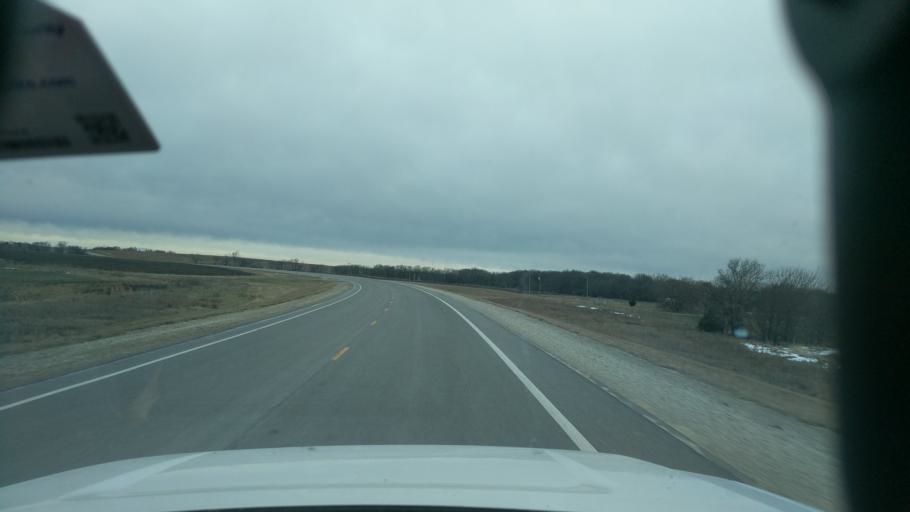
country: US
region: Kansas
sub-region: Marion County
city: Marion
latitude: 38.4225
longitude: -96.9649
